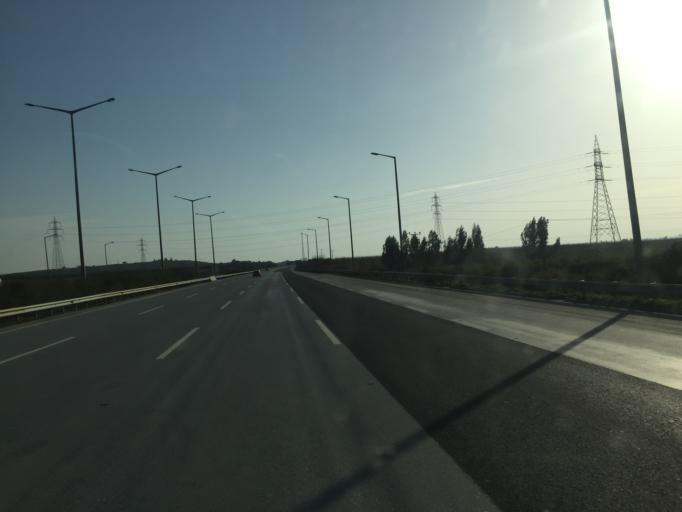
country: TR
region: Mersin
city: Yenice
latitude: 37.0235
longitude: 35.0677
